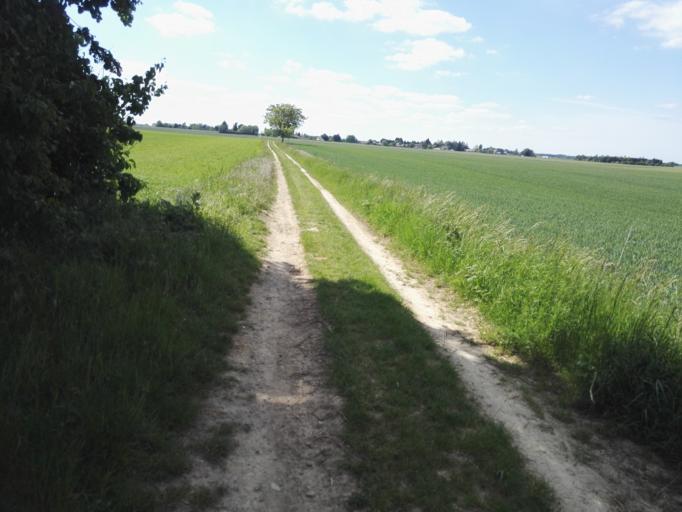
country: FR
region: Haute-Normandie
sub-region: Departement de l'Eure
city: Menilles
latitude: 49.0039
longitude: 1.3214
